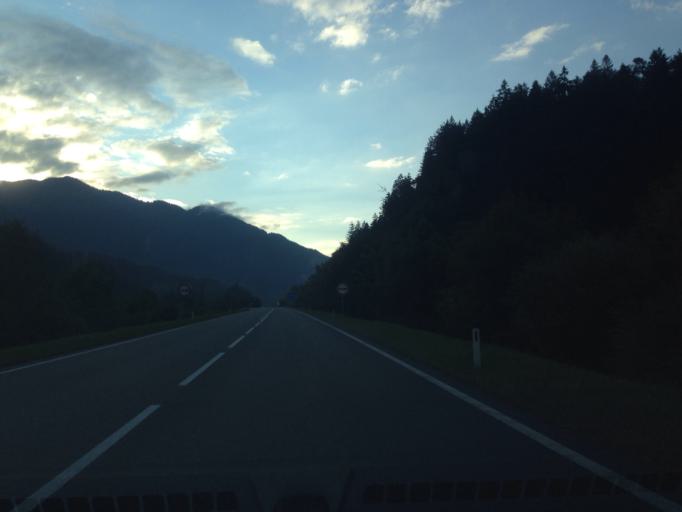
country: AT
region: Tyrol
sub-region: Politischer Bezirk Reutte
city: Pflach
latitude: 47.5269
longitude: 10.6953
